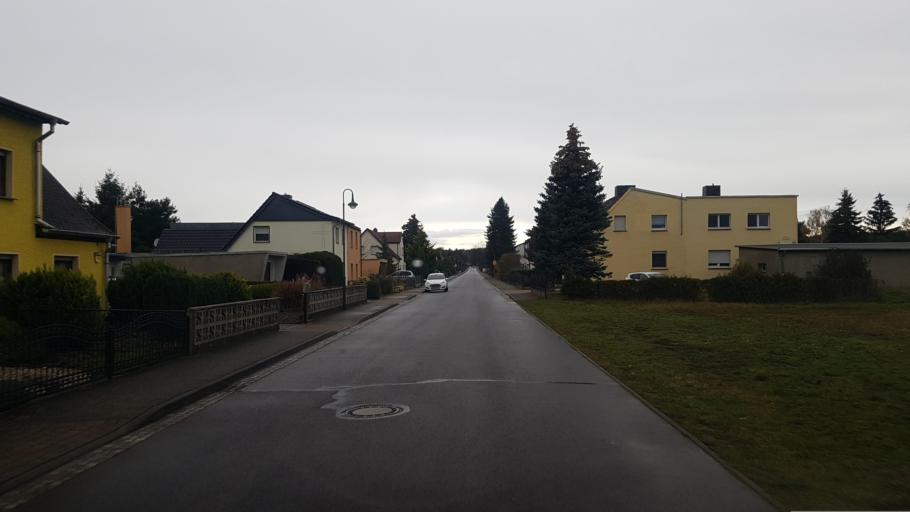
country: DE
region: Saxony-Anhalt
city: Abtsdorf
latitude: 51.8769
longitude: 12.7402
